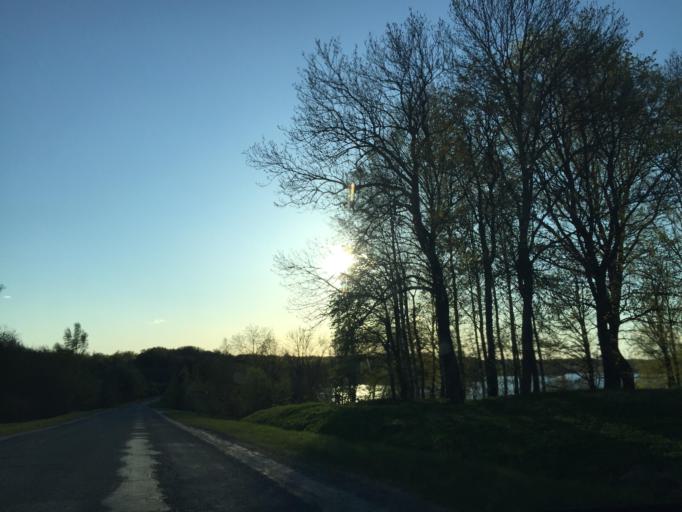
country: LV
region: Ergli
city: Ergli
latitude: 56.8756
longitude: 25.7010
